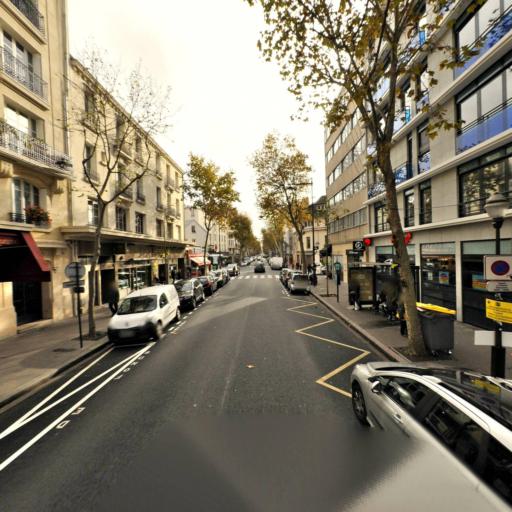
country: FR
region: Ile-de-France
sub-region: Departement des Hauts-de-Seine
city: Boulogne-Billancourt
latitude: 48.8418
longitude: 2.2388
